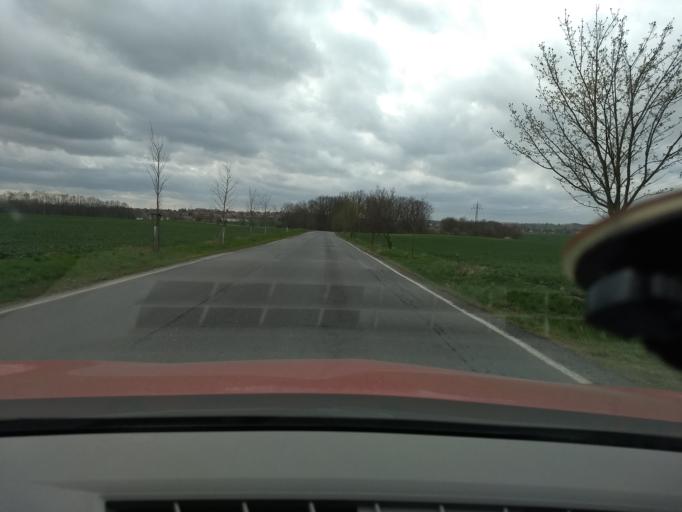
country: CZ
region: Central Bohemia
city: Unhost'
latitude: 50.0775
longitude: 14.1441
